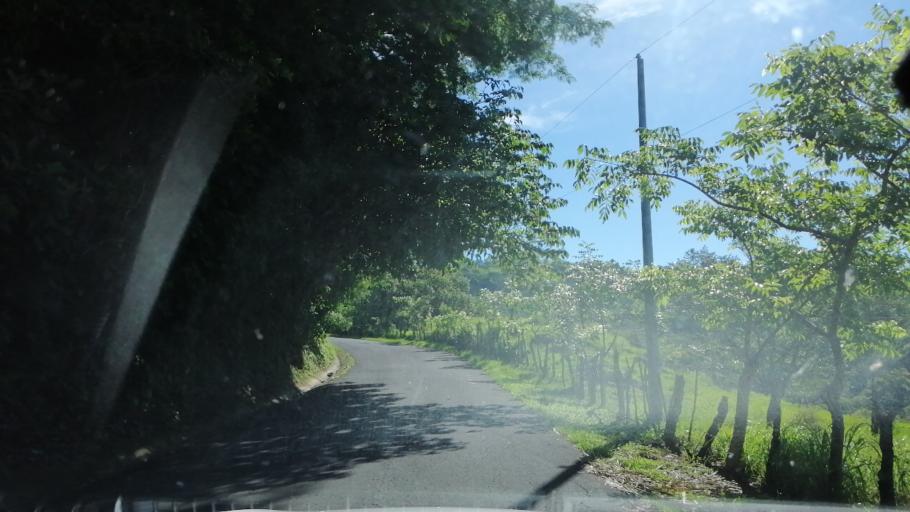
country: SV
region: Morazan
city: Corinto
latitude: 13.8080
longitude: -88.0027
